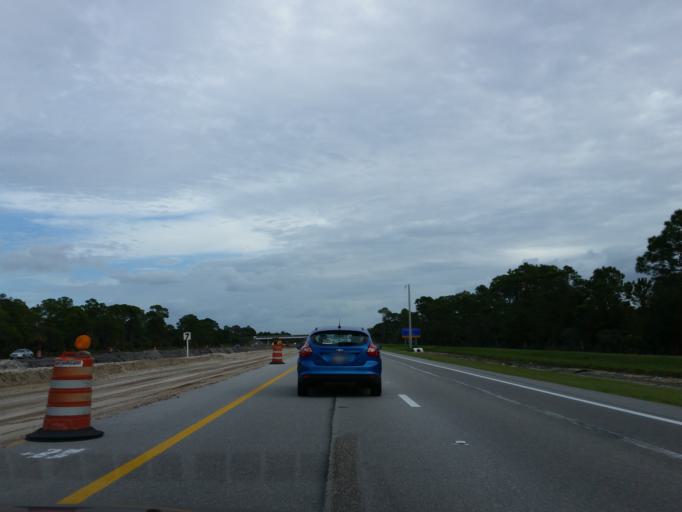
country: US
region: Florida
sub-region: Sarasota County
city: Warm Mineral Springs
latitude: 27.0995
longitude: -82.2381
